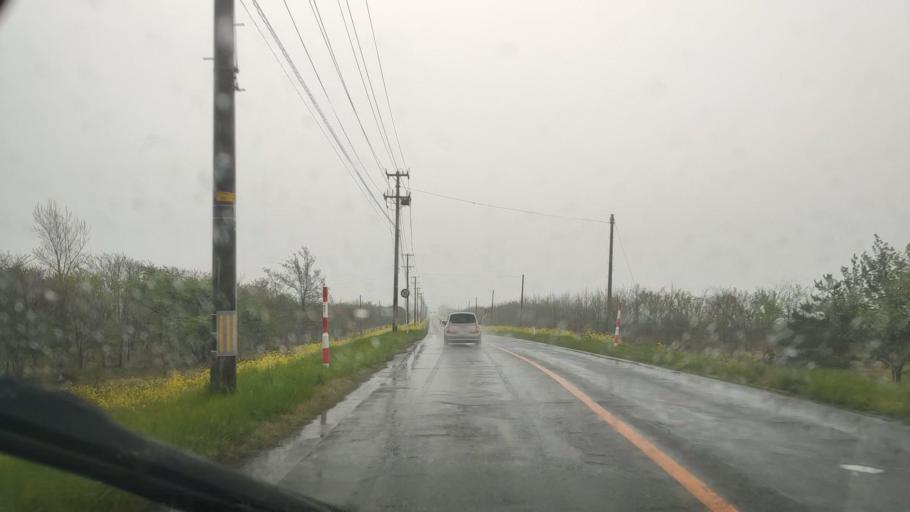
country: JP
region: Akita
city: Tenno
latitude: 40.0007
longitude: 139.9464
